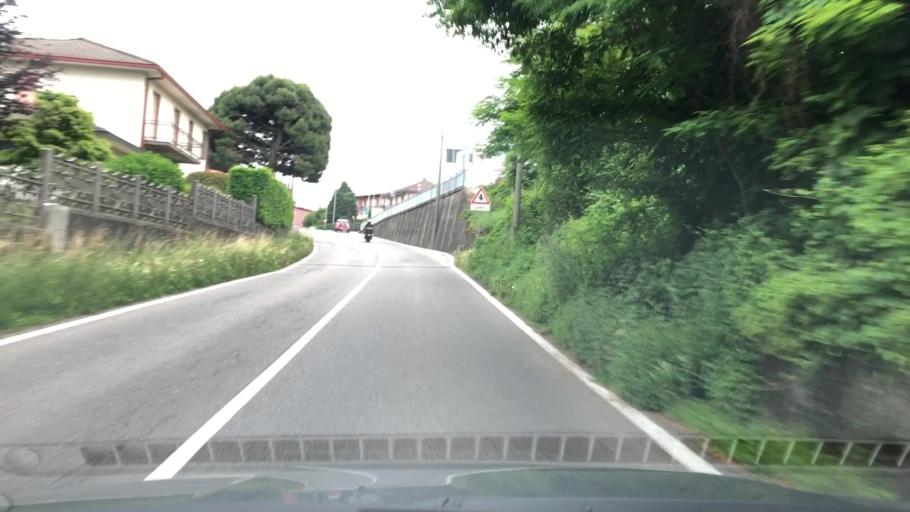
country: IT
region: Lombardy
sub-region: Provincia di Como
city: Casnate Con Bernate
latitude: 45.7647
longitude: 9.0743
